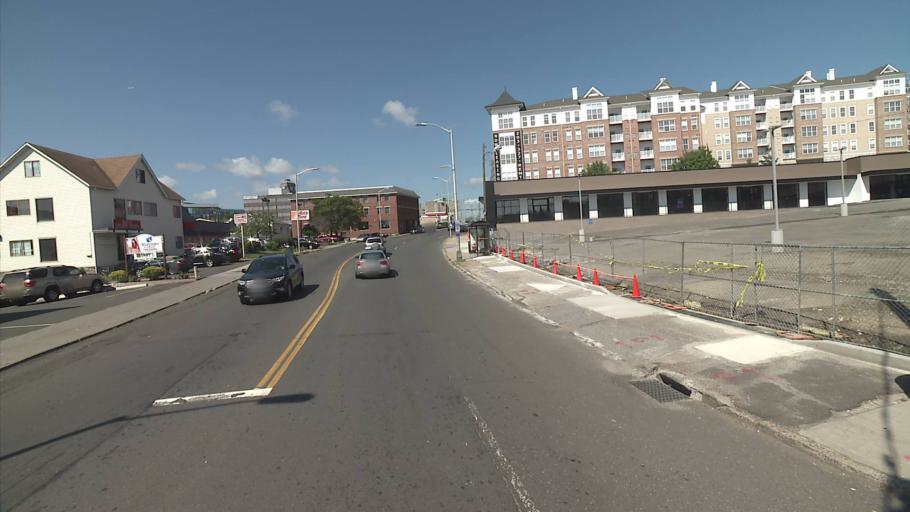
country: US
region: Connecticut
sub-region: Fairfield County
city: Stamford
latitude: 41.0553
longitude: -73.5274
